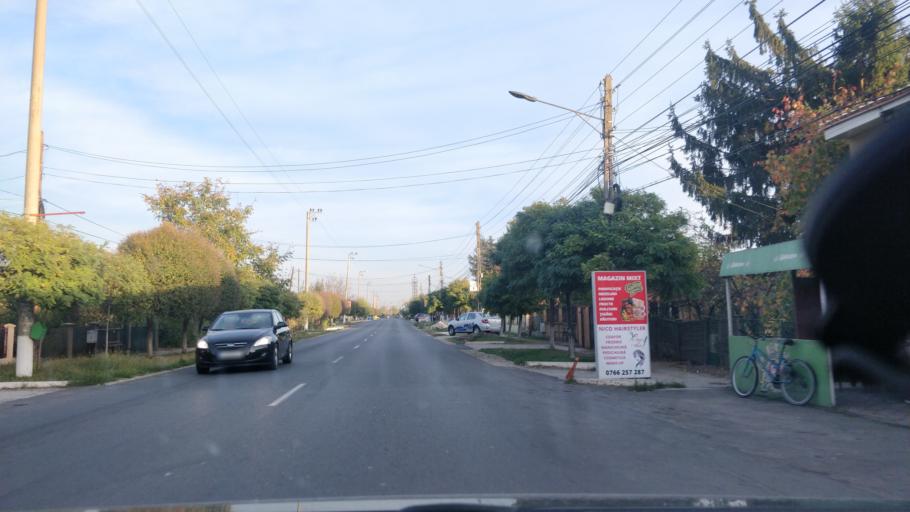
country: RO
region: Ilfov
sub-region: Comuna Ciorogarla
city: Ciorogarla
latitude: 44.4433
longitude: 25.8921
